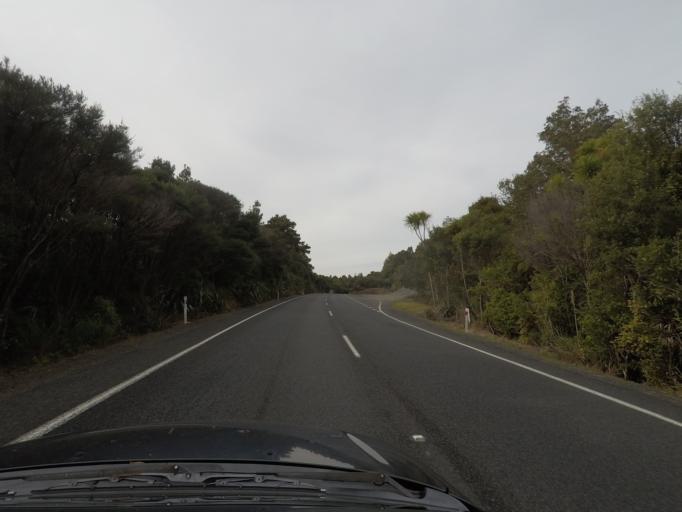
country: NZ
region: Auckland
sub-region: Auckland
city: Titirangi
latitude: -36.9437
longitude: 174.5320
